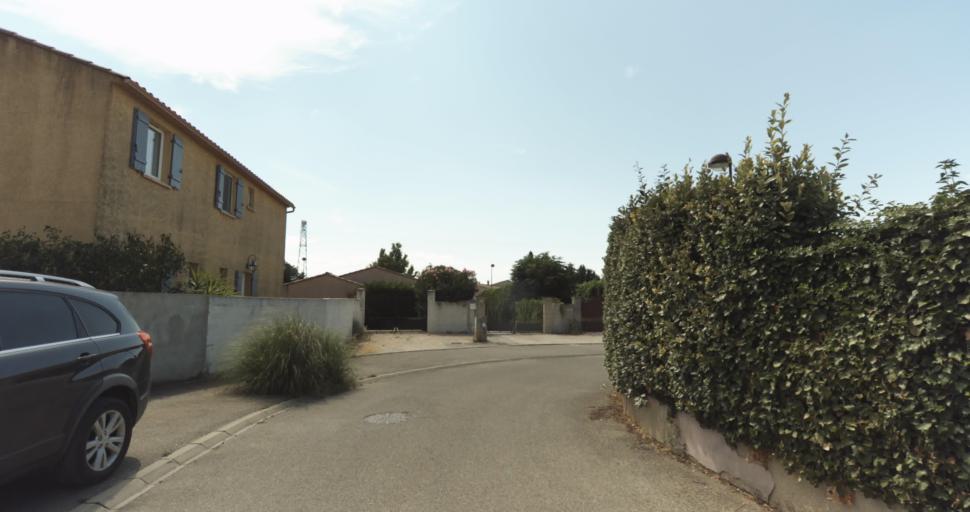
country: FR
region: Provence-Alpes-Cote d'Azur
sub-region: Departement du Vaucluse
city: Monteux
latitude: 44.0333
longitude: 4.9796
